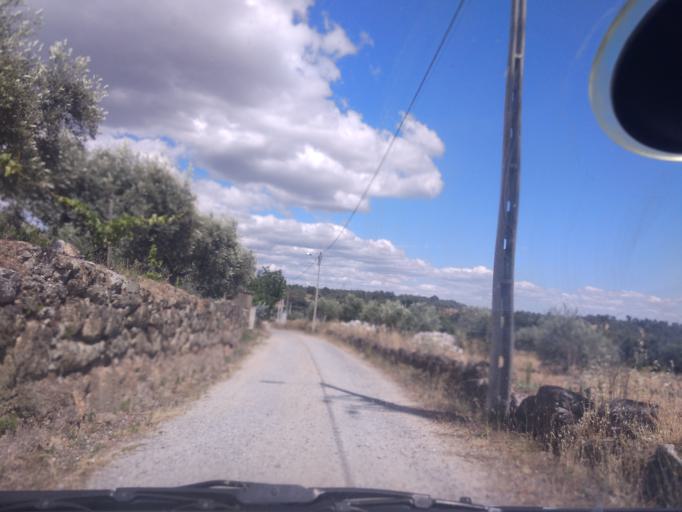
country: PT
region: Castelo Branco
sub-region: Concelho do Fundao
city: Fundao
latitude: 40.2062
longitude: -7.4385
